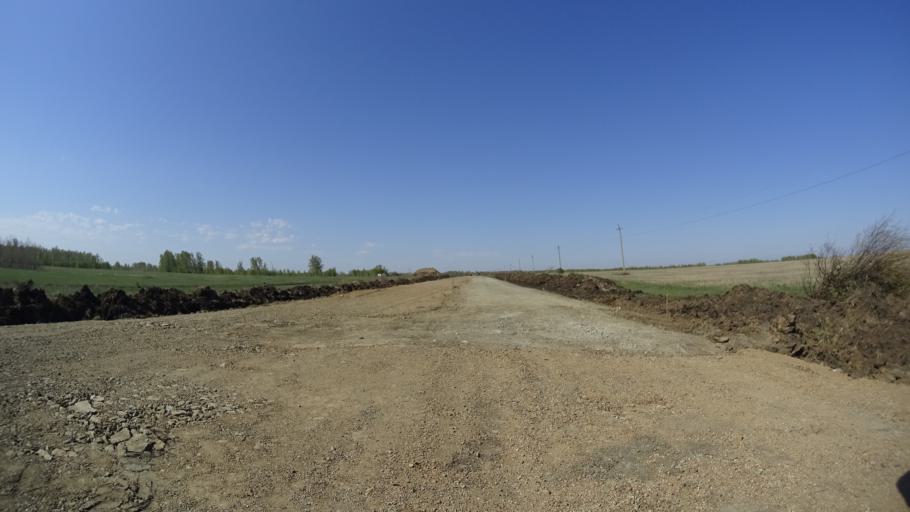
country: RU
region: Chelyabinsk
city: Troitsk
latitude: 54.1836
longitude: 61.4896
